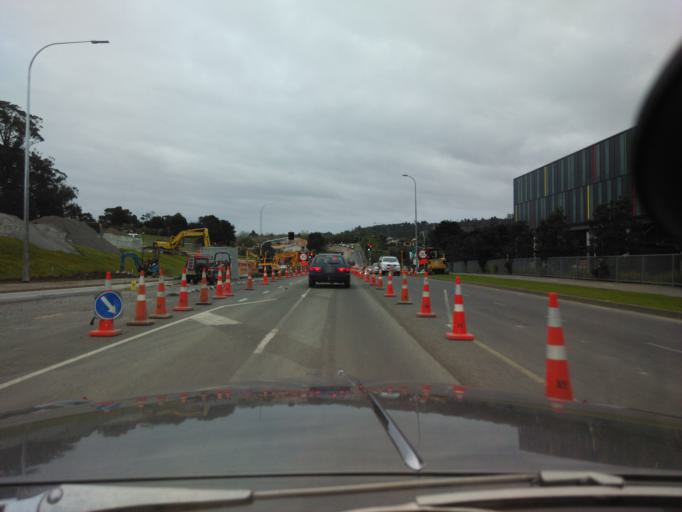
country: NZ
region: Auckland
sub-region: Auckland
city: Rothesay Bay
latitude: -36.7307
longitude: 174.6967
